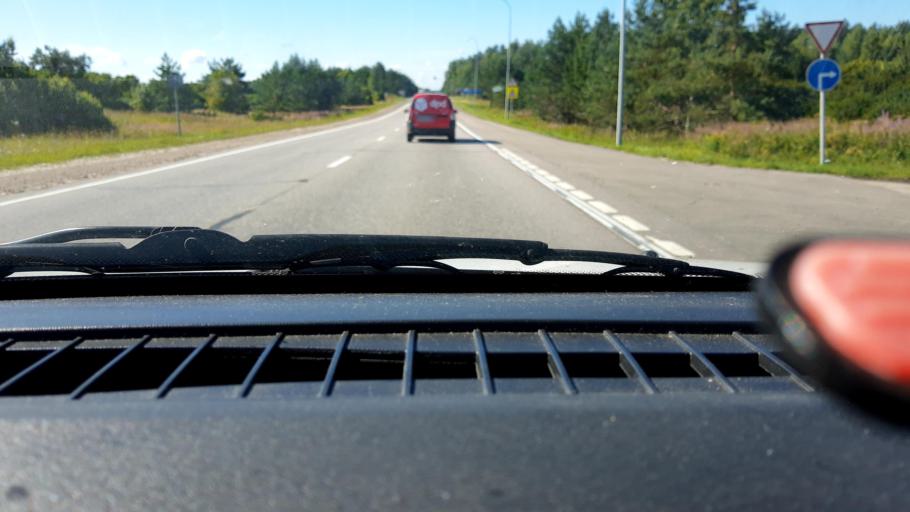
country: RU
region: Nizjnij Novgorod
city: Surovatikha
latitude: 55.6417
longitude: 43.9896
